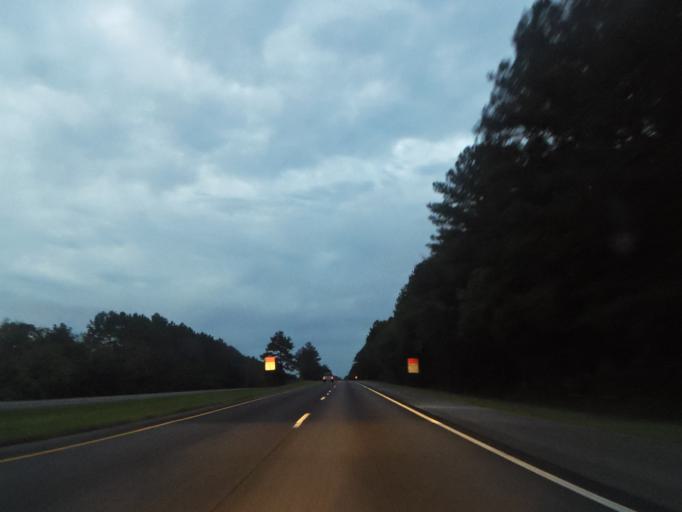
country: US
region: Alabama
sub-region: DeKalb County
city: Crossville
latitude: 34.1887
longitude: -85.9535
